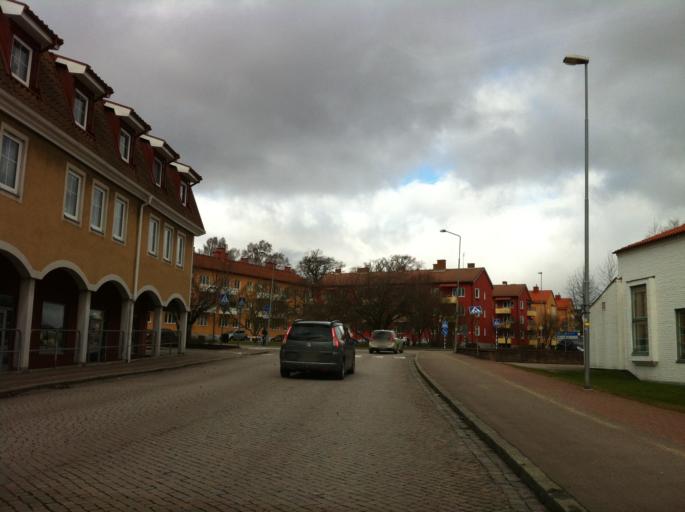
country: SE
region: Skane
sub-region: Bromolla Kommun
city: Bromoella
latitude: 56.0380
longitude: 14.3876
